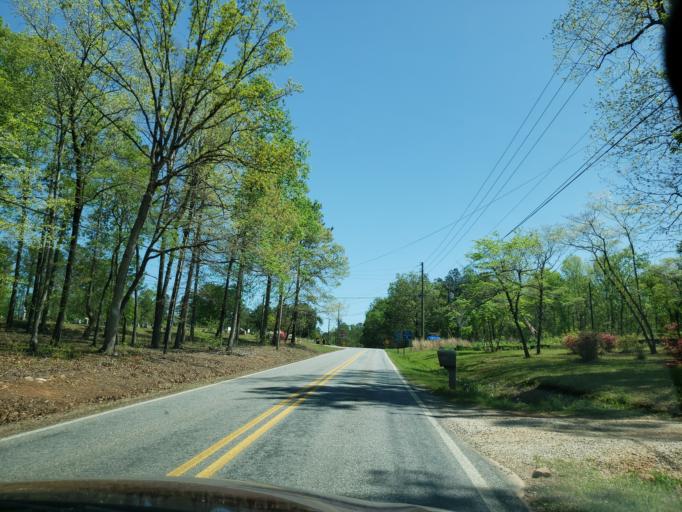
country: US
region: Alabama
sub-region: Tallapoosa County
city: Dadeville
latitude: 32.6968
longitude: -85.8526
